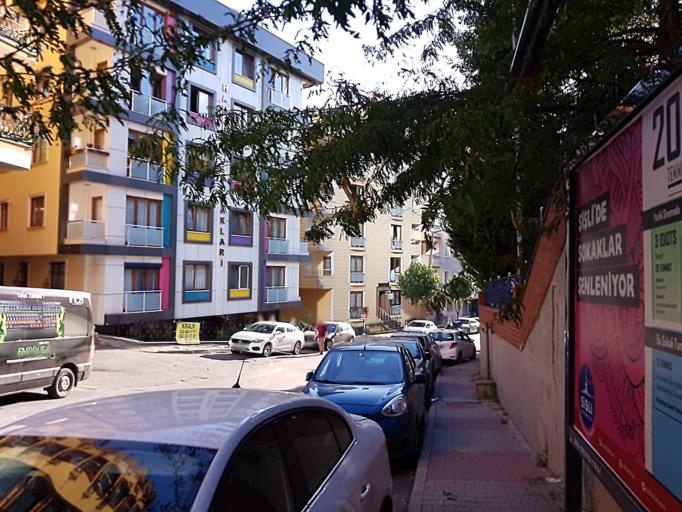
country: TR
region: Istanbul
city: Sisli
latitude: 41.0716
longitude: 29.0069
